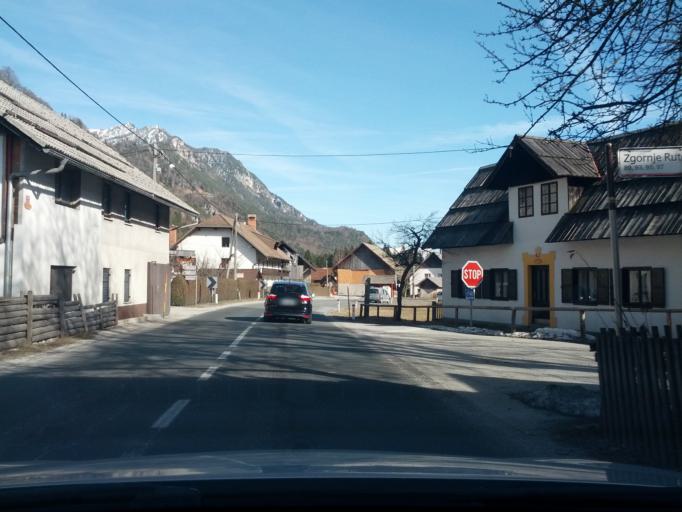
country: SI
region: Kranjska Gora
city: Kranjska Gora
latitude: 46.4862
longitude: 13.8275
